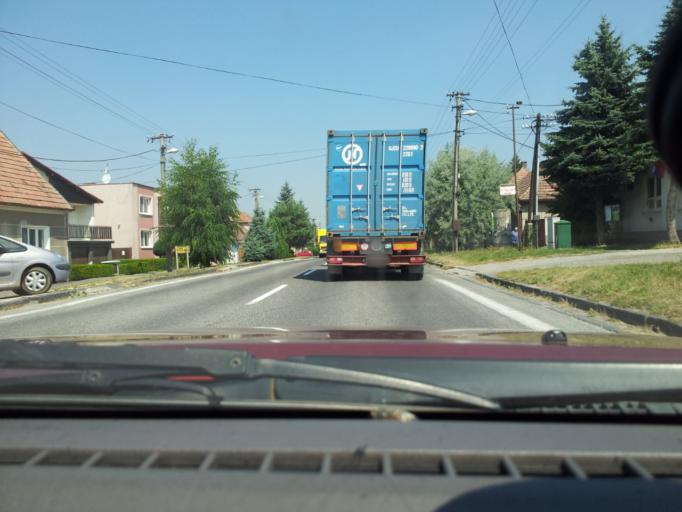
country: SK
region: Trnavsky
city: Smolenice
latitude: 48.5043
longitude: 17.4802
